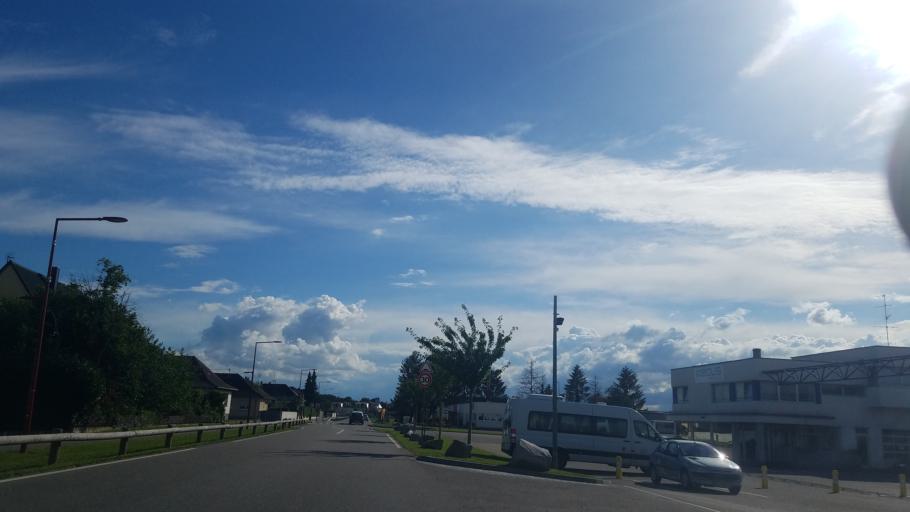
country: FR
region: Alsace
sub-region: Departement du Bas-Rhin
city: Soufflenheim
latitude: 48.8178
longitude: 7.9626
